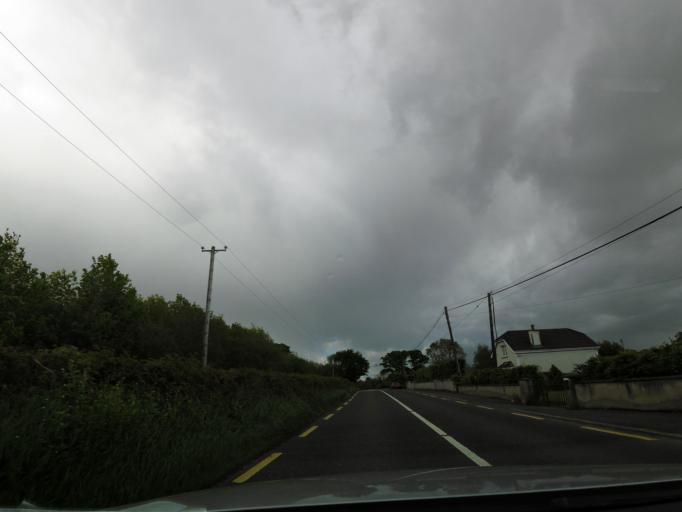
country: IE
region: Munster
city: Thurles
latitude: 52.7082
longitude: -7.8249
